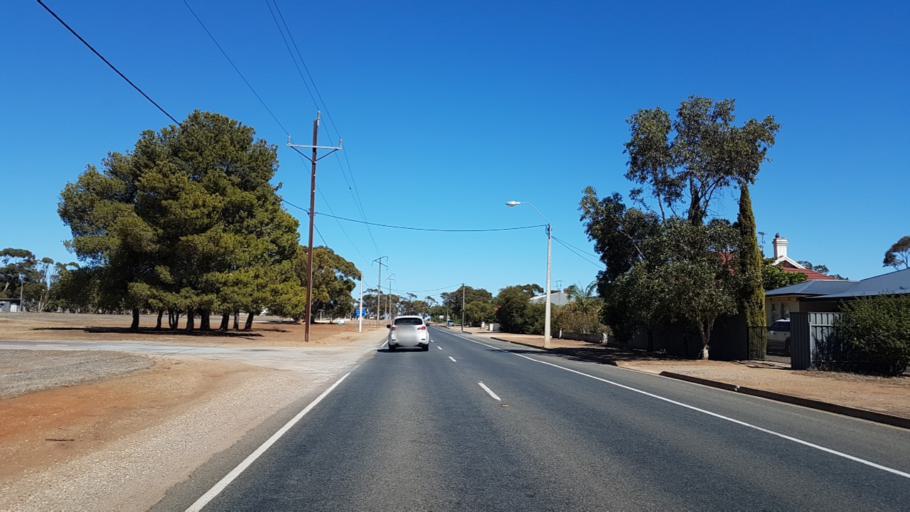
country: AU
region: South Australia
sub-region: Copper Coast
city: Kadina
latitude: -34.0378
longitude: 137.9034
